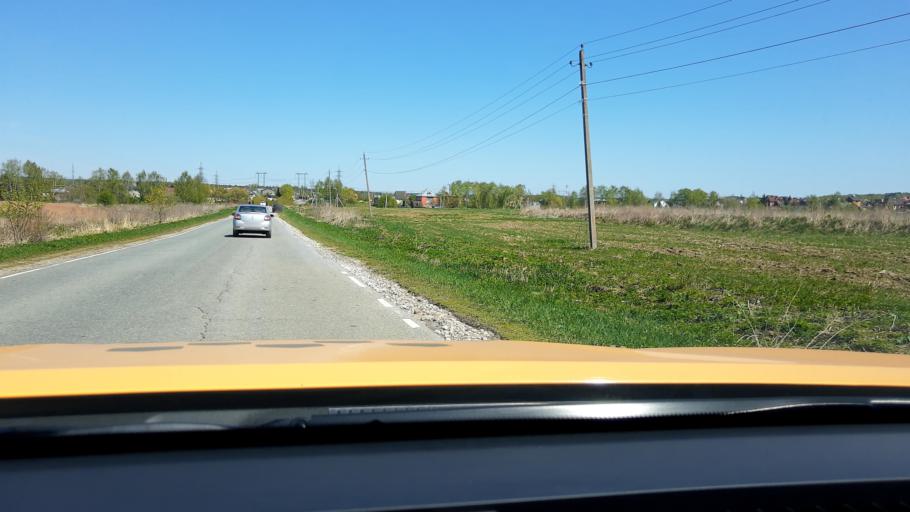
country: RU
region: Moskovskaya
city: Gorki-Leninskiye
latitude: 55.4692
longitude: 37.8347
